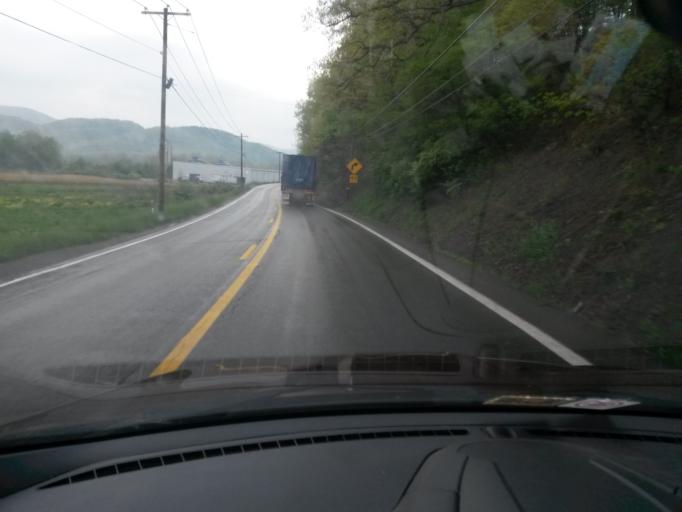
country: US
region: West Virginia
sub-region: Randolph County
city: Elkins
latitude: 38.8317
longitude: -79.8738
